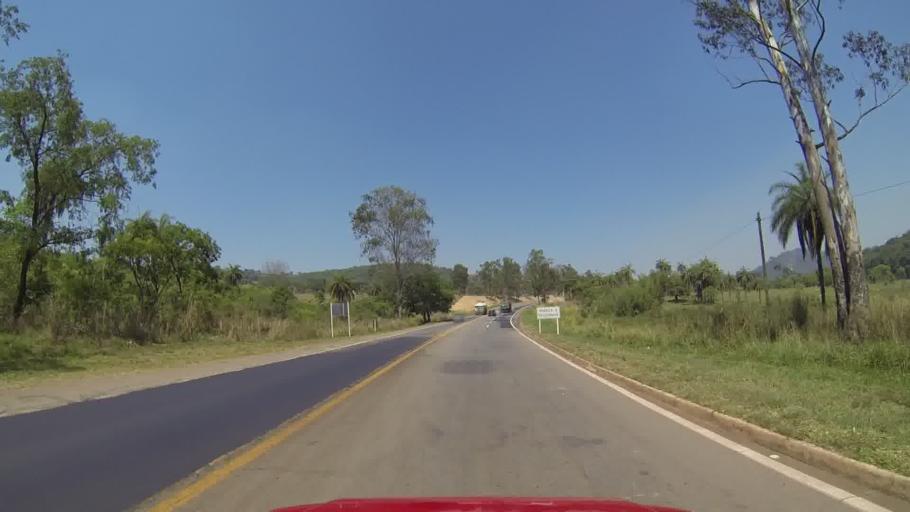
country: BR
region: Minas Gerais
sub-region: Mateus Leme
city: Mateus Leme
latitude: -20.0248
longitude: -44.5032
